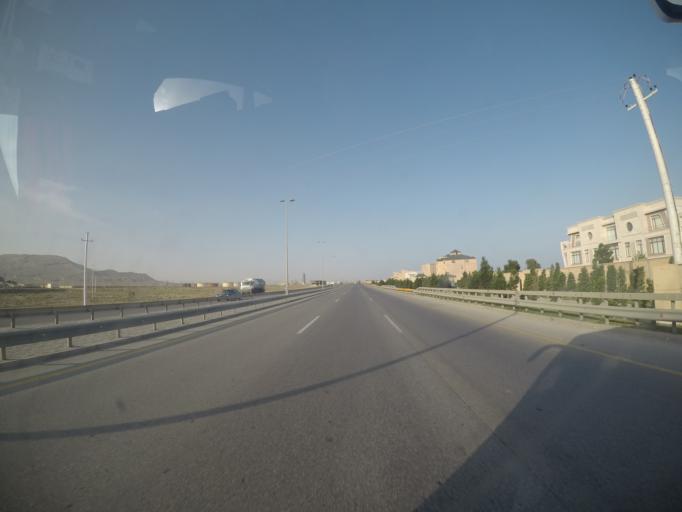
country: AZ
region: Baki
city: Korgoz
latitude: 40.2040
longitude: 49.5271
